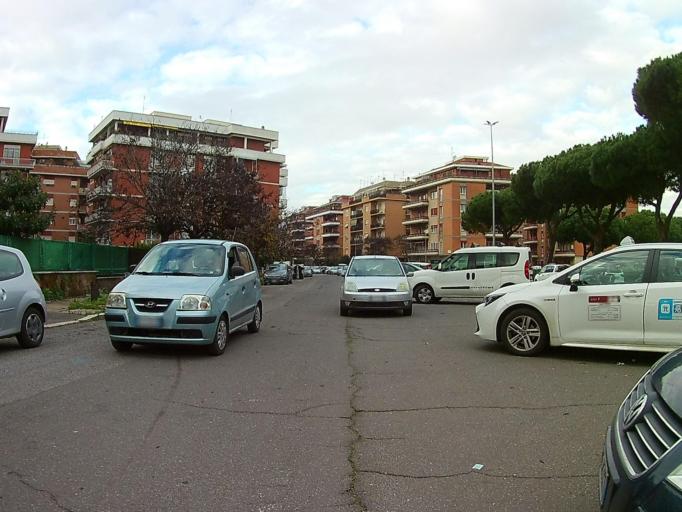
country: IT
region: Latium
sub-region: Citta metropolitana di Roma Capitale
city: Lido di Ostia
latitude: 41.7298
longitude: 12.2939
